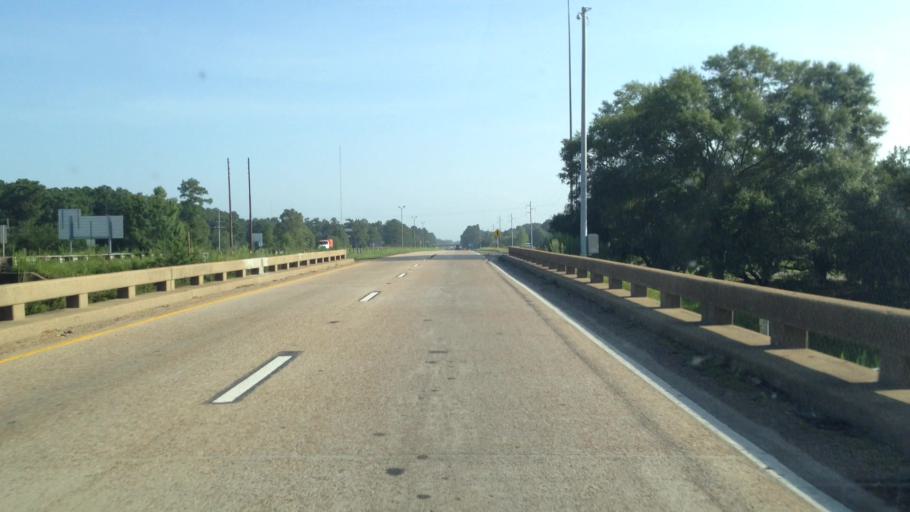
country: US
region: Mississippi
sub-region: Pike County
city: Summit
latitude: 31.2598
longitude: -90.4791
